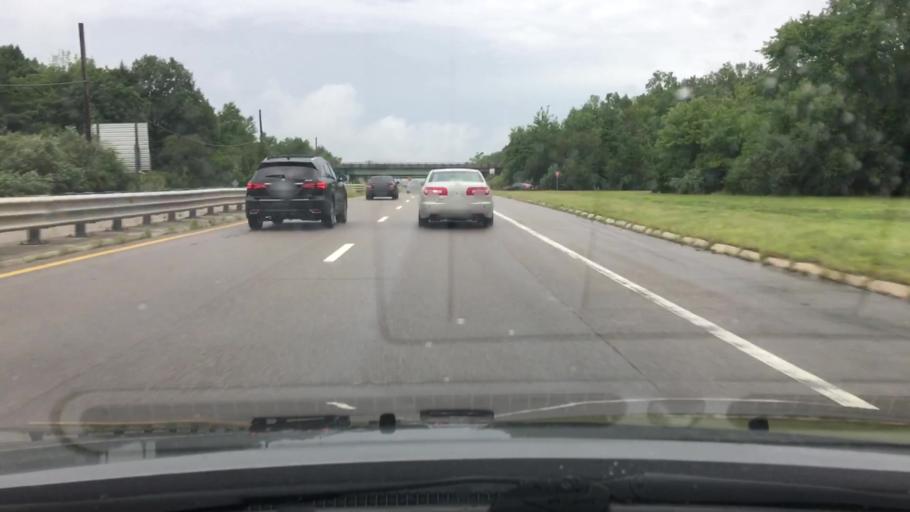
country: US
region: Massachusetts
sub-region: Norfolk County
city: Plainville
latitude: 41.9472
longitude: -71.3465
